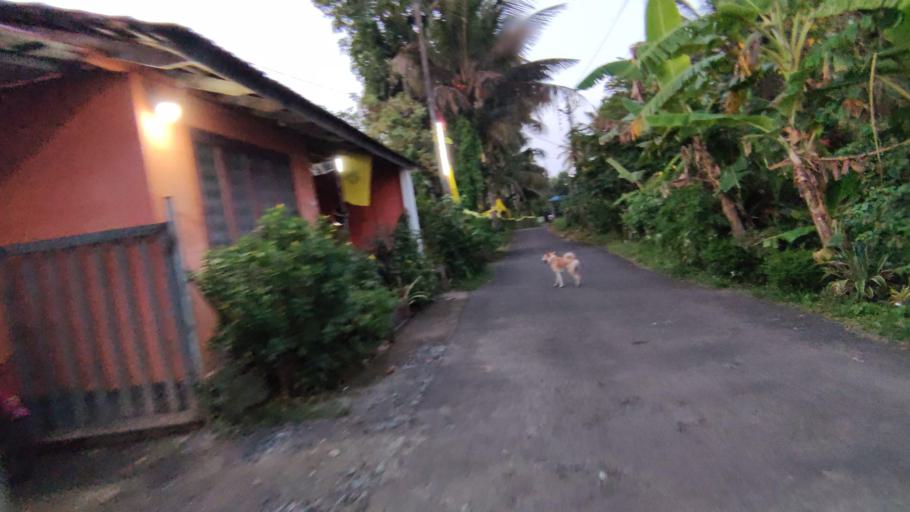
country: IN
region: Kerala
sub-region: Kottayam
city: Kottayam
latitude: 9.5732
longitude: 76.4350
